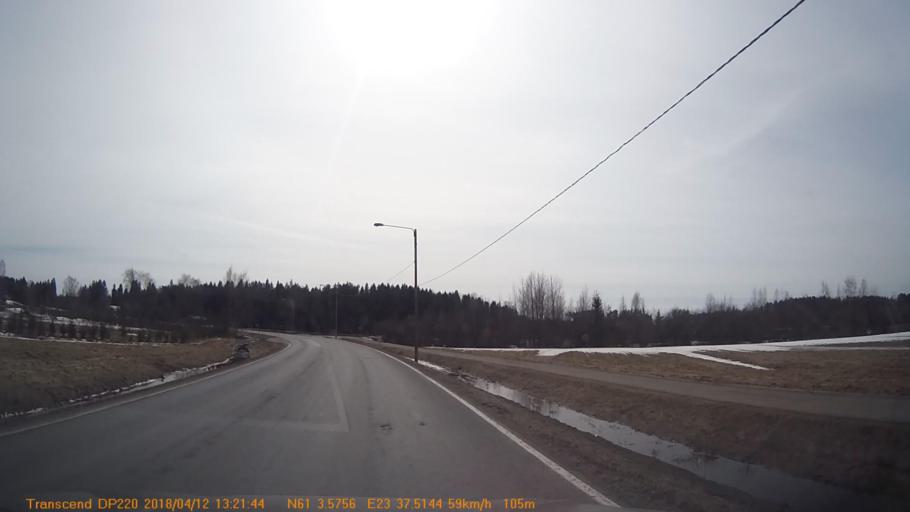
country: FI
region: Pirkanmaa
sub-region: Etelae-Pirkanmaa
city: Urjala
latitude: 61.0588
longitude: 23.6249
